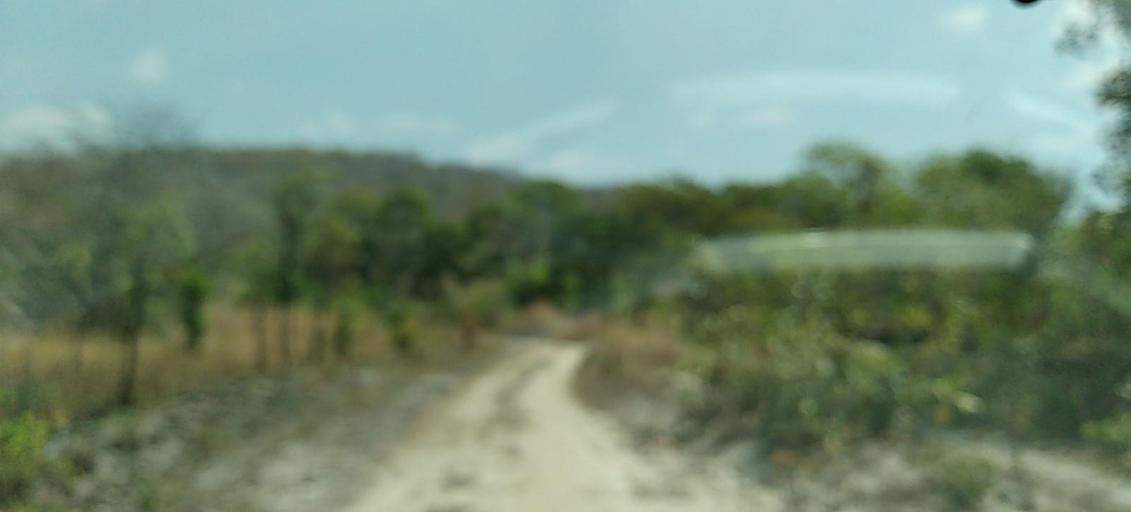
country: ZM
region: North-Western
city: Kasempa
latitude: -13.5269
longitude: 25.8230
